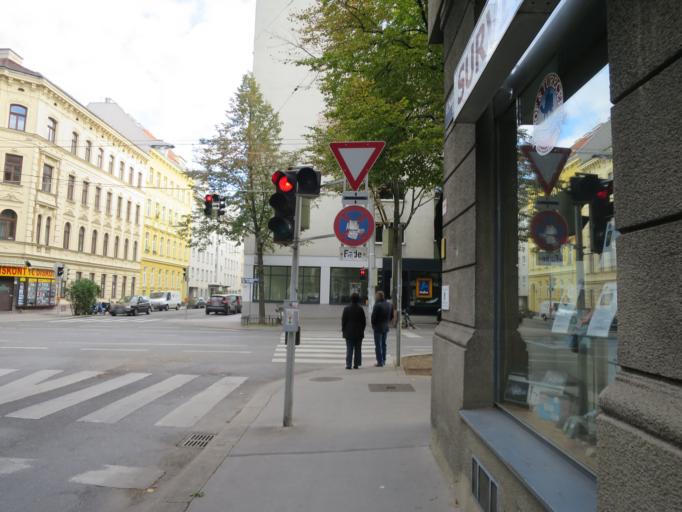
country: AT
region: Vienna
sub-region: Wien Stadt
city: Vienna
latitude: 48.2003
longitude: 16.3303
